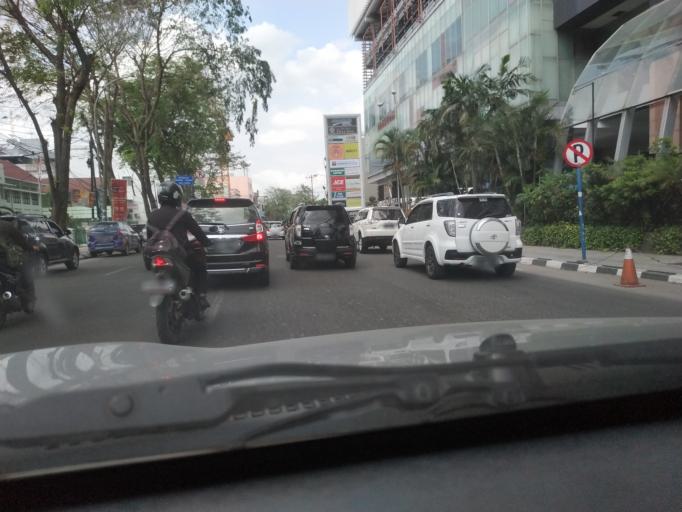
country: ID
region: North Sumatra
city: Medan
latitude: 3.5848
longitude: 98.6670
